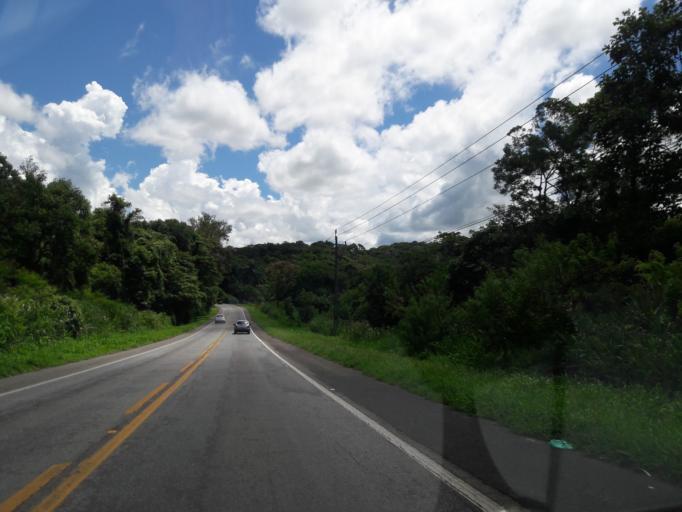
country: BR
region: Parana
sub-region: Antonina
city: Antonina
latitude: -25.4423
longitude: -48.7917
